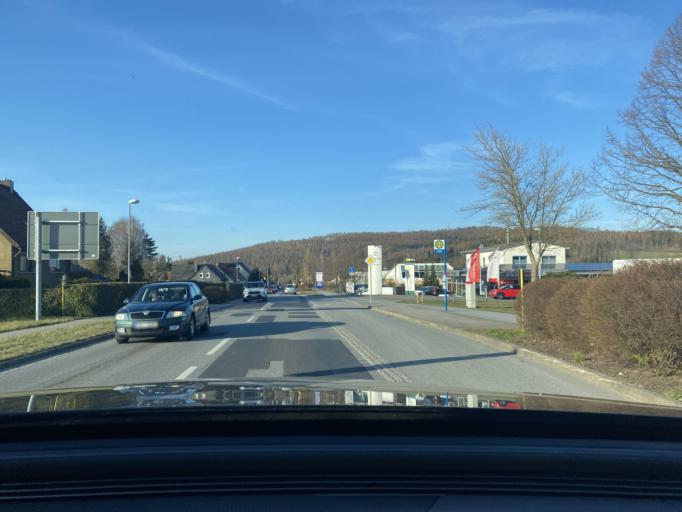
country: DE
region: Saxony
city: Sohland
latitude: 51.0562
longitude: 14.4282
